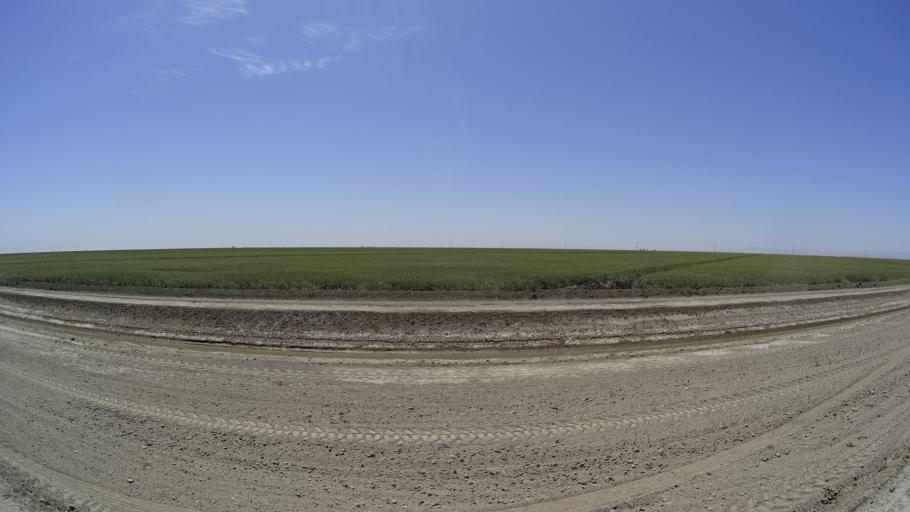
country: US
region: California
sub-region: Kings County
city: Corcoran
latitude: 36.1233
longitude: -119.6884
